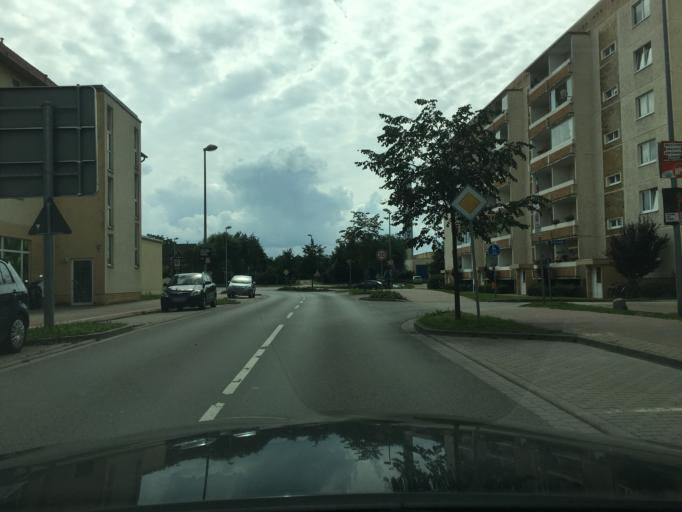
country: DE
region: Mecklenburg-Vorpommern
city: Waren
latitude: 53.5092
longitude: 12.7021
